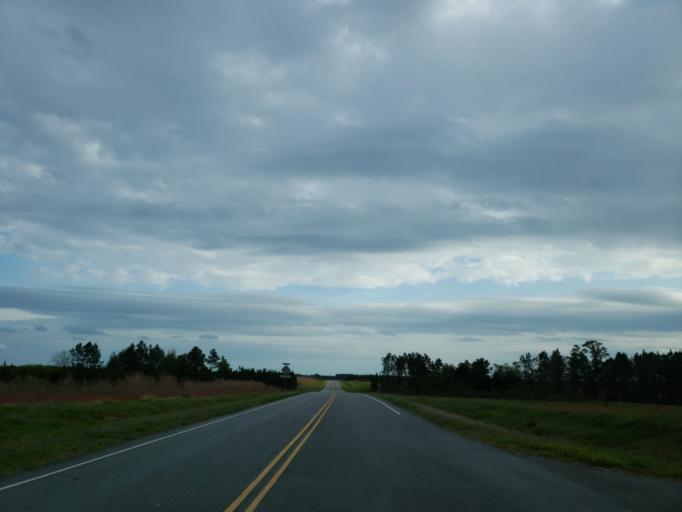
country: US
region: Georgia
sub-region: Dooly County
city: Vienna
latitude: 32.1201
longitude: -83.7561
